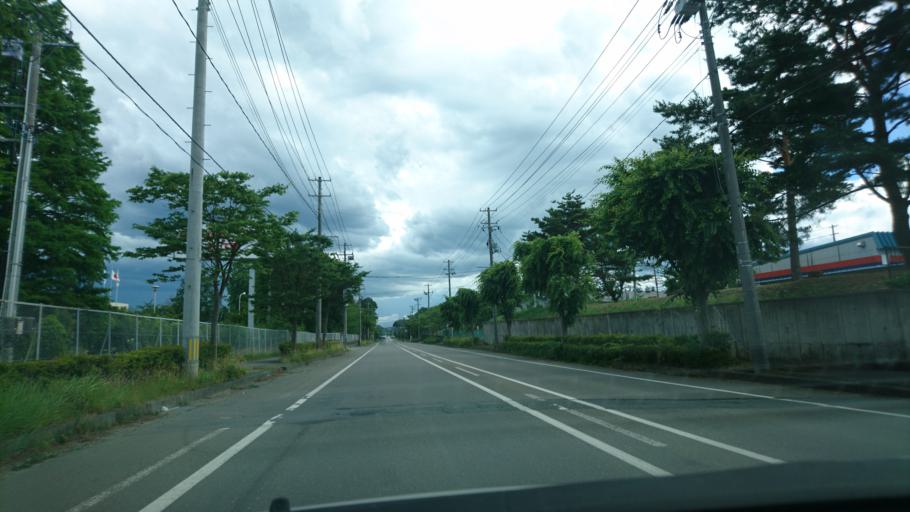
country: JP
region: Iwate
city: Kitakami
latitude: 39.3315
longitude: 141.1280
